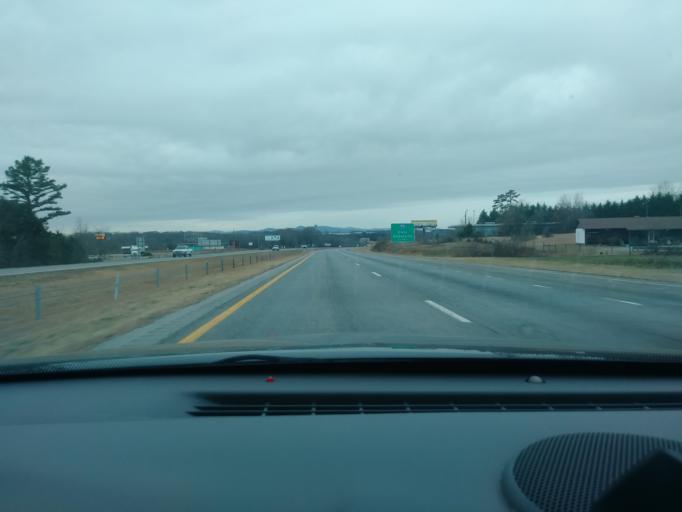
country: US
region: North Carolina
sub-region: Yadkin County
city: Jonesville
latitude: 36.1195
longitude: -80.8000
